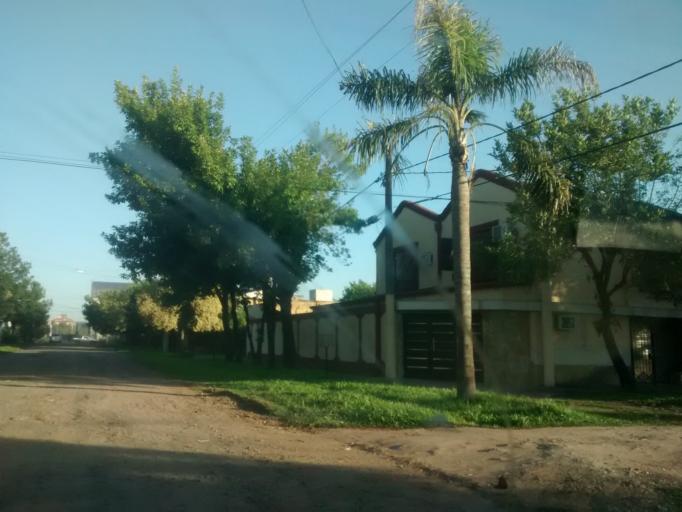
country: AR
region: Chaco
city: Resistencia
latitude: -27.4702
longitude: -58.9811
